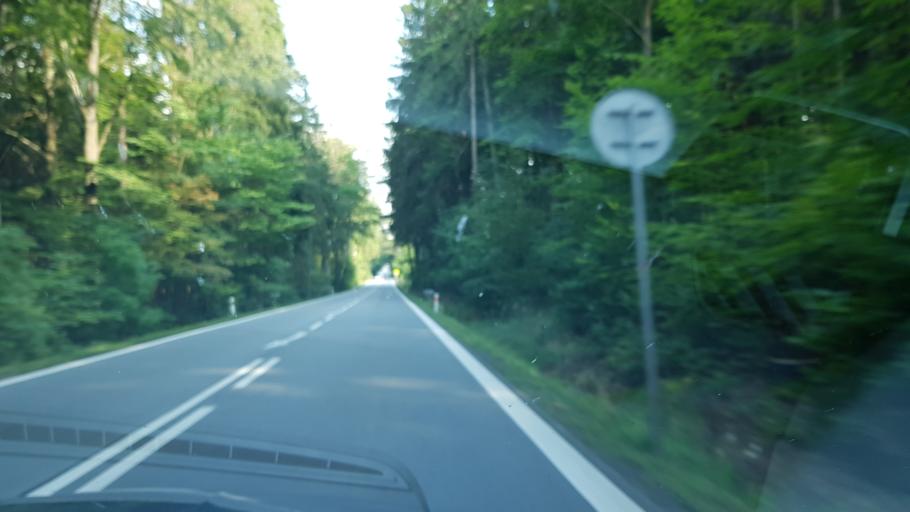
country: CZ
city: Vamberk
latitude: 50.1187
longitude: 16.3494
